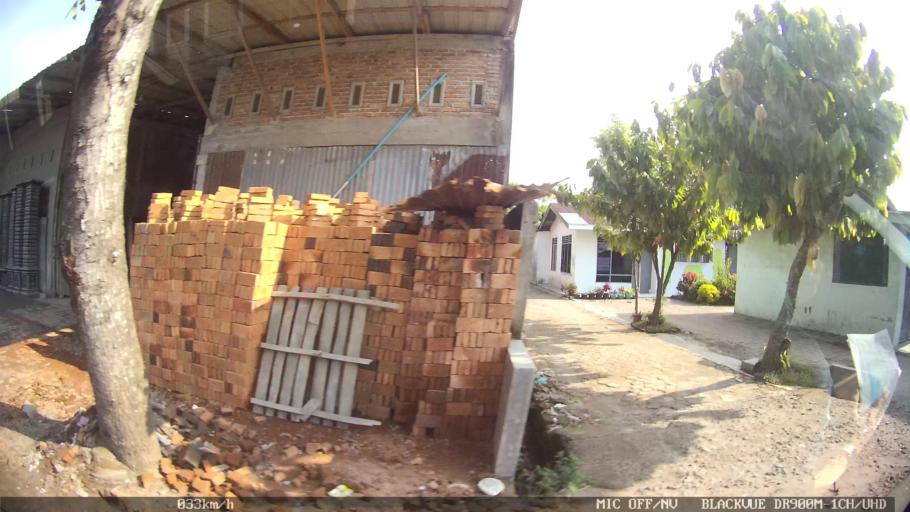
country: ID
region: North Sumatra
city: Percut
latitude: 3.5939
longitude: 98.7823
